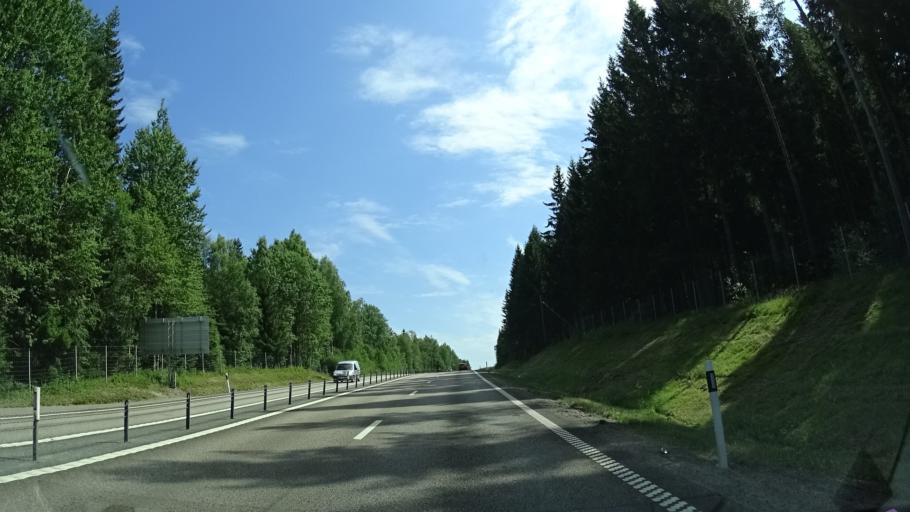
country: SE
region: Vaermland
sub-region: Kristinehamns Kommun
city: Bjorneborg
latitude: 59.3119
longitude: 14.2222
